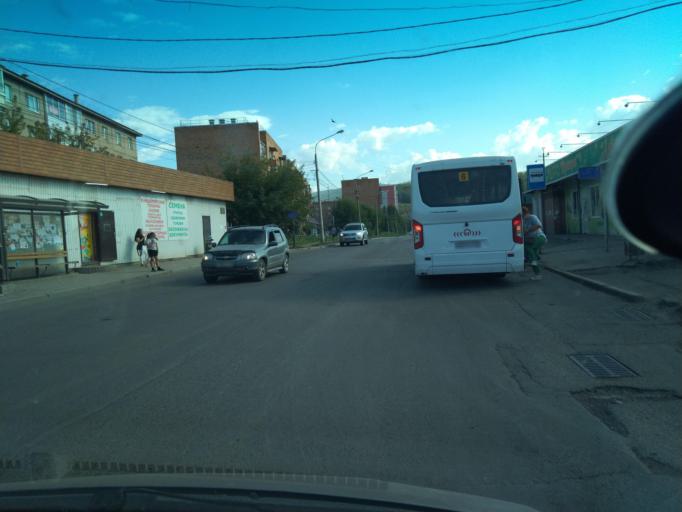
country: RU
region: Krasnoyarskiy
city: Krasnoyarsk
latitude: 55.9735
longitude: 92.9365
